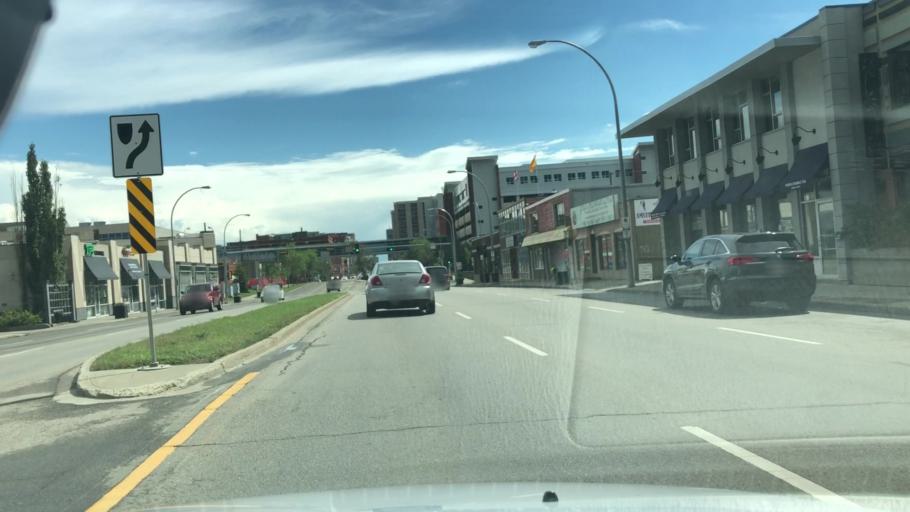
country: CA
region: Alberta
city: Edmonton
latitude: 53.5493
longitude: -113.5085
